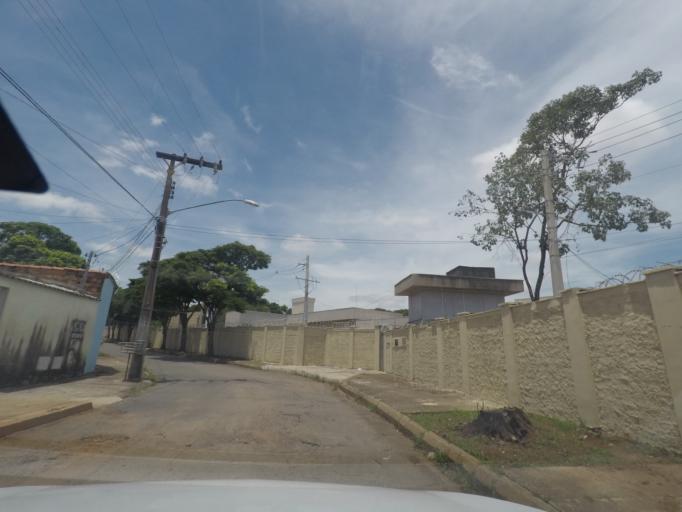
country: BR
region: Goias
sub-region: Goiania
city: Goiania
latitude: -16.6602
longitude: -49.1983
